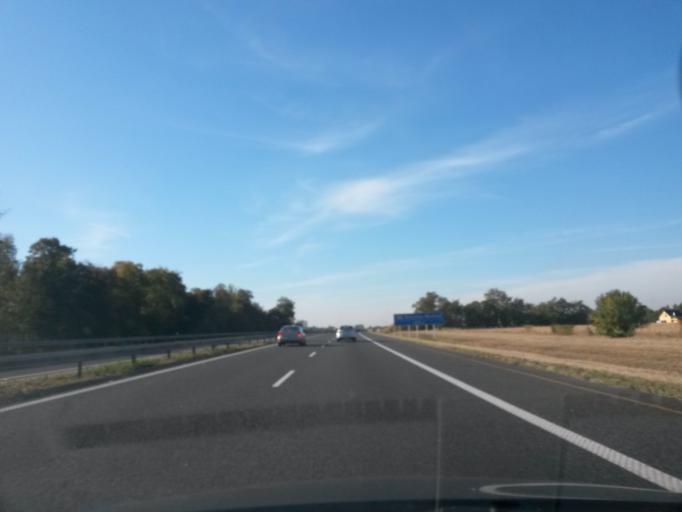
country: PL
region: Lower Silesian Voivodeship
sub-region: Powiat wroclawski
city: Zorawina
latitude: 50.9441
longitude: 17.0949
